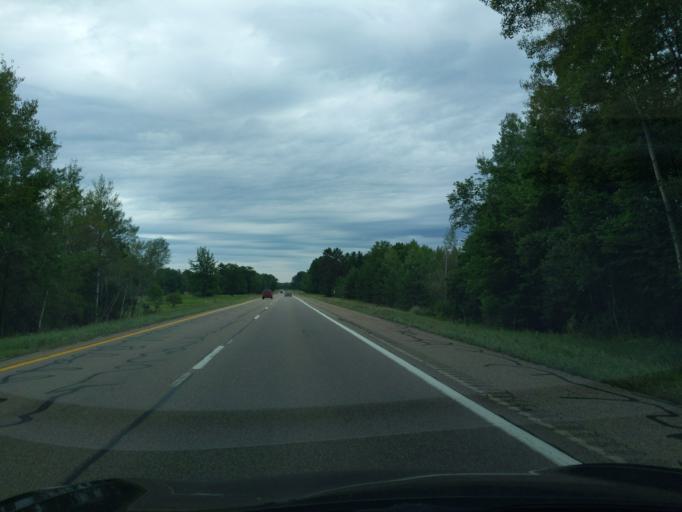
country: US
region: Michigan
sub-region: Roscommon County
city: Houghton Lake
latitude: 44.3213
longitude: -84.8071
